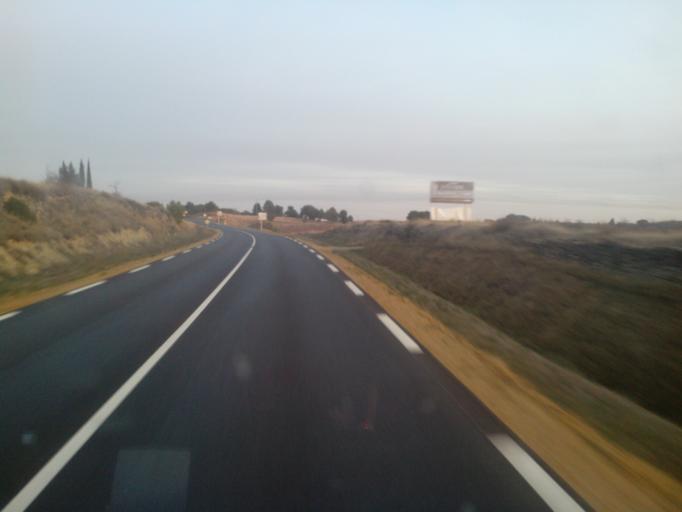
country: FR
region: Languedoc-Roussillon
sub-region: Departement de l'Aude
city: Ginestas
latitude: 43.2842
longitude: 2.8391
